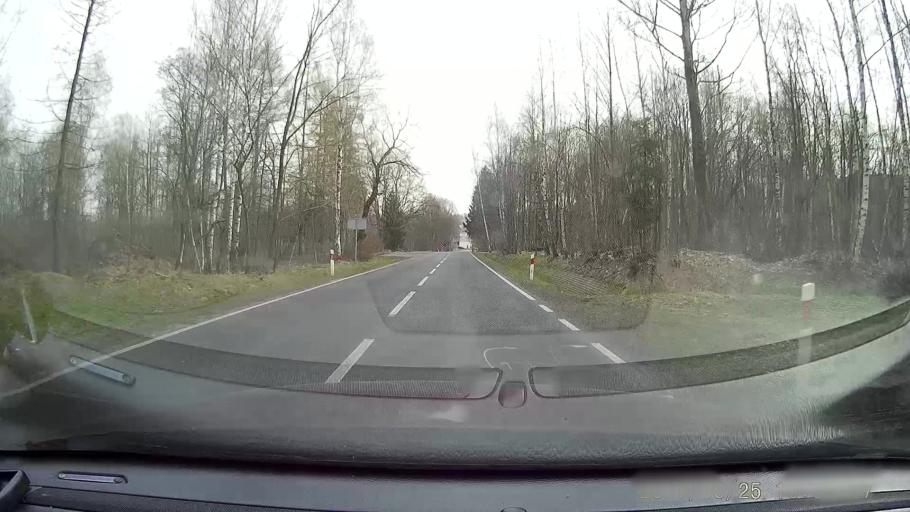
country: PL
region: Lower Silesian Voivodeship
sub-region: Powiat lubanski
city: Swieradow-Zdroj
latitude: 50.9305
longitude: 15.3500
